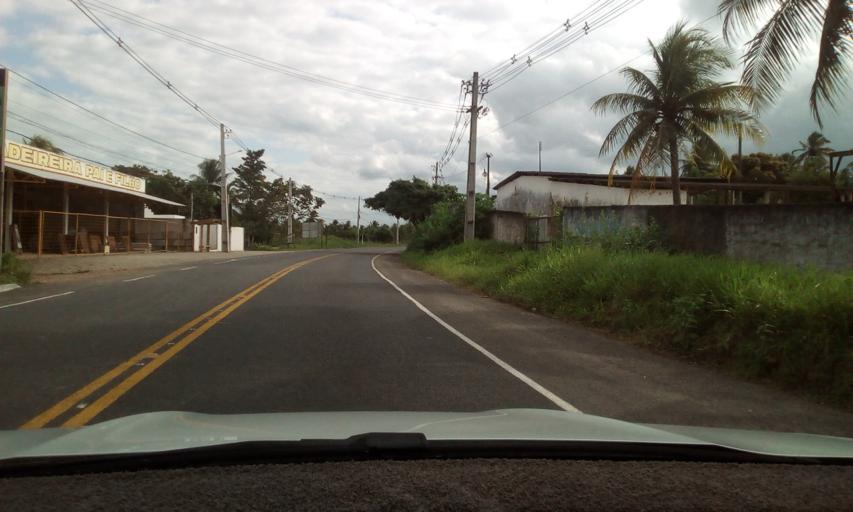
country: BR
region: Paraiba
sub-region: Mamanguape
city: Mamanguape
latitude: -6.8302
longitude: -35.1127
